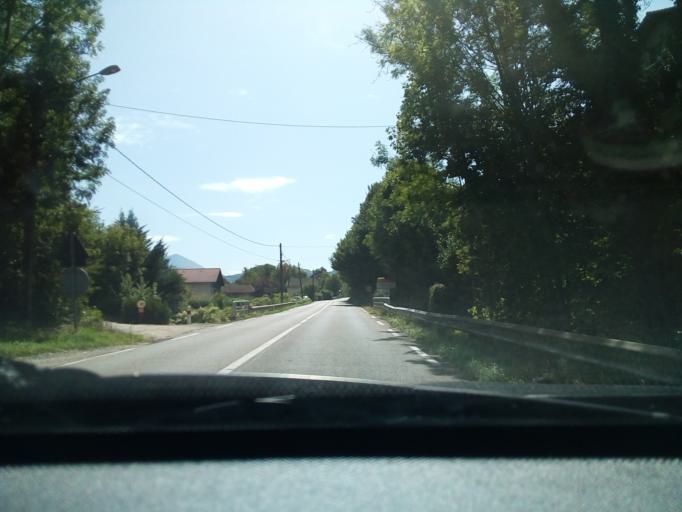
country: FR
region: Rhone-Alpes
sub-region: Departement de l'Isere
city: Poisat
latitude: 45.1418
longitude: 5.7697
